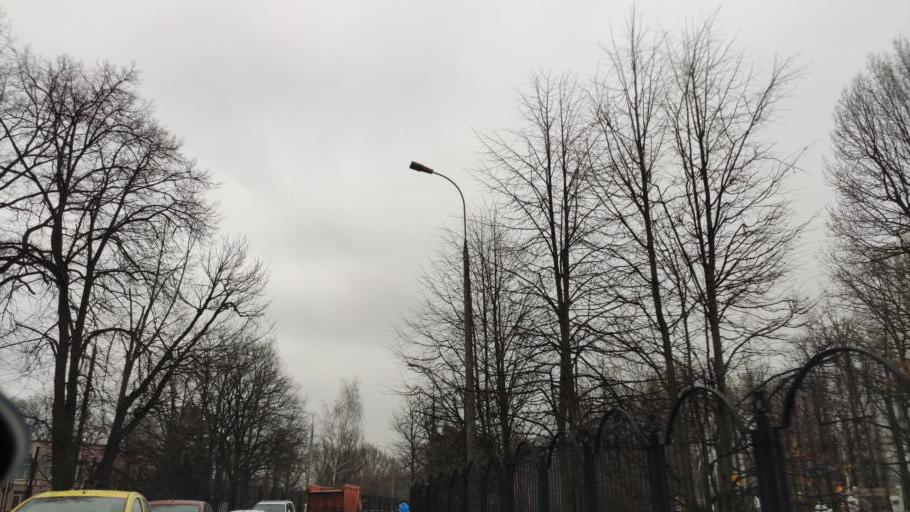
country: RU
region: Moskovskaya
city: Bol'shaya Setun'
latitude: 55.7452
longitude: 37.4307
